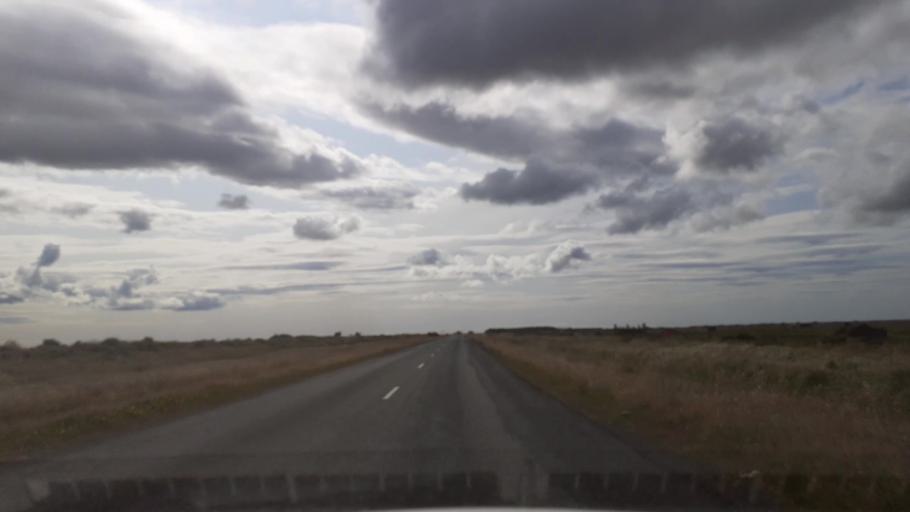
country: IS
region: South
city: Vestmannaeyjar
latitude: 63.8222
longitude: -20.4273
